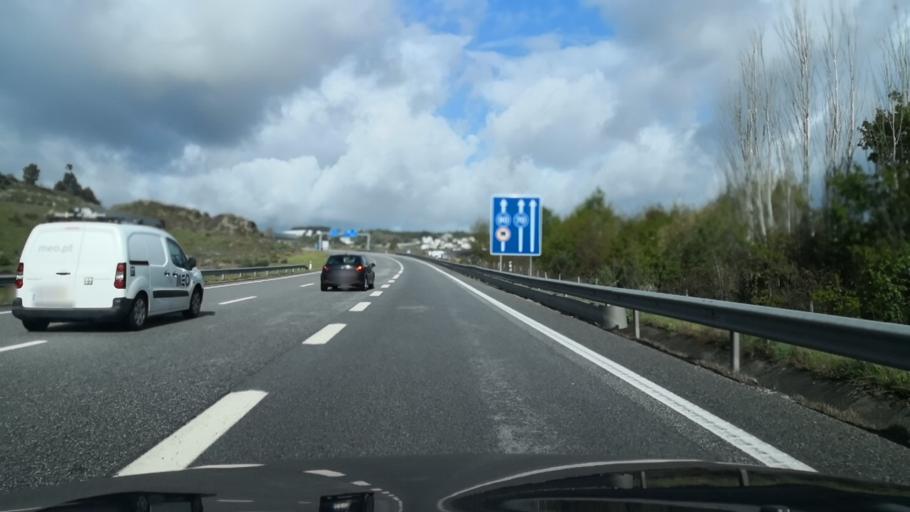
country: PT
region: Viseu
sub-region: Viseu
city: Rio de Loba
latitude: 40.6332
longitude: -7.8278
